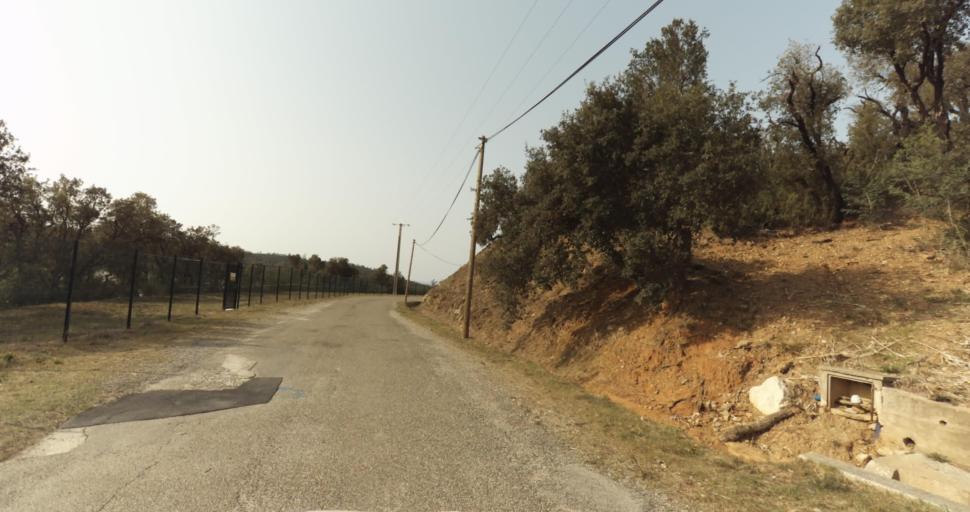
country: FR
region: Provence-Alpes-Cote d'Azur
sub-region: Departement du Var
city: Bormes-les-Mimosas
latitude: 43.1436
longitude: 6.2924
